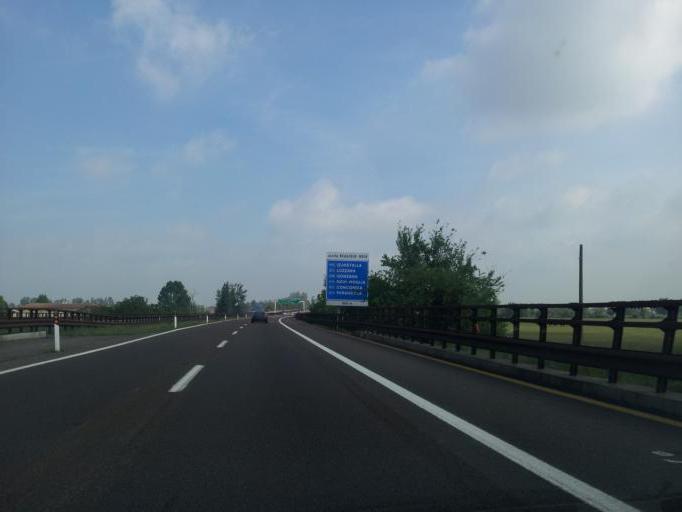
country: IT
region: Emilia-Romagna
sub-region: Provincia di Reggio Emilia
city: Rolo
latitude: 44.9035
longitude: 10.8486
